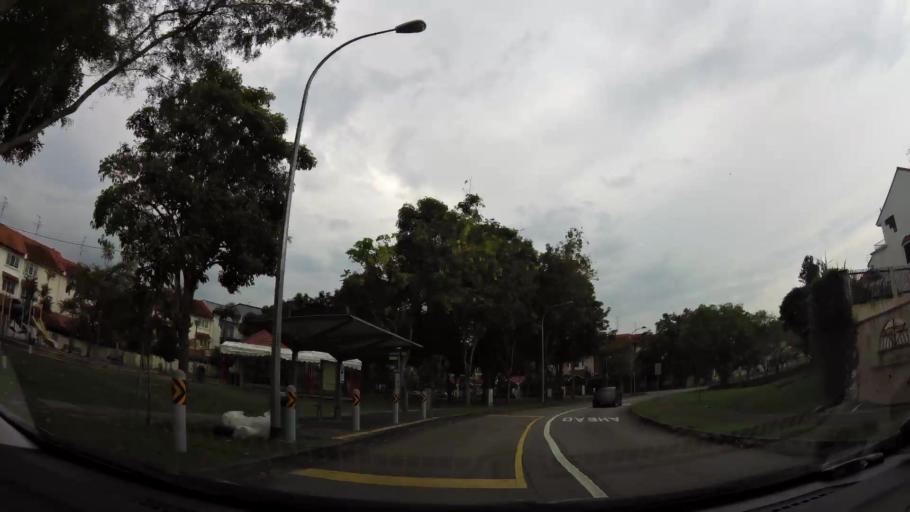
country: MY
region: Johor
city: Kampung Pasir Gudang Baru
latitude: 1.3898
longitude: 103.8386
